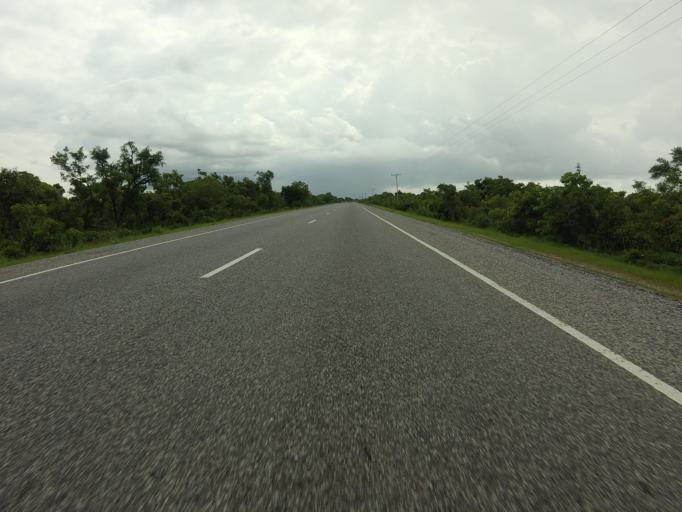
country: GH
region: Northern
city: Tamale
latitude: 9.1344
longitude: -1.3301
